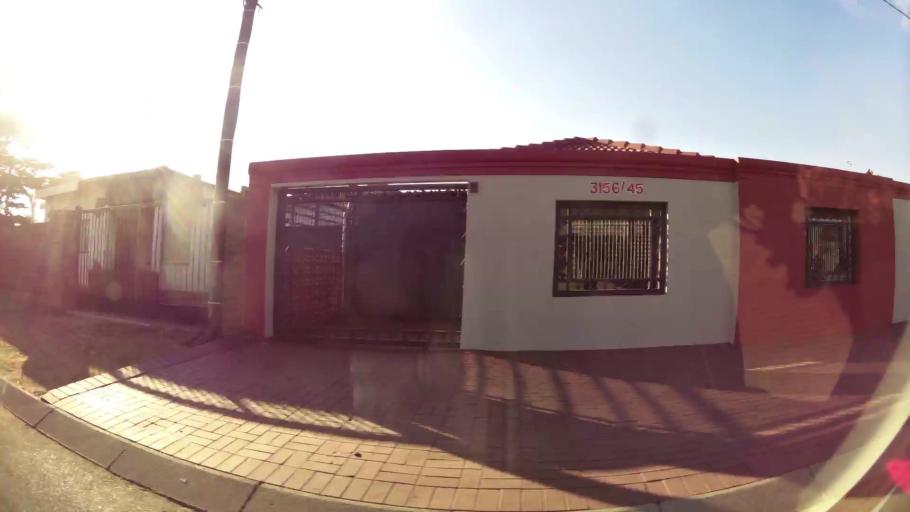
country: ZA
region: Gauteng
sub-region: City of Johannesburg Metropolitan Municipality
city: Soweto
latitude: -26.2677
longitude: 27.8721
